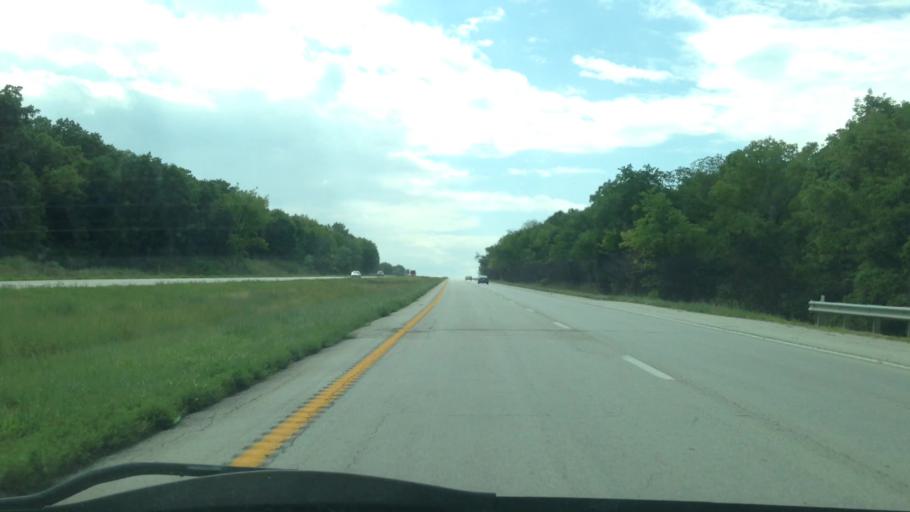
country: US
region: Missouri
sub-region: Marion County
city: Hannibal
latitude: 39.7440
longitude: -91.4306
